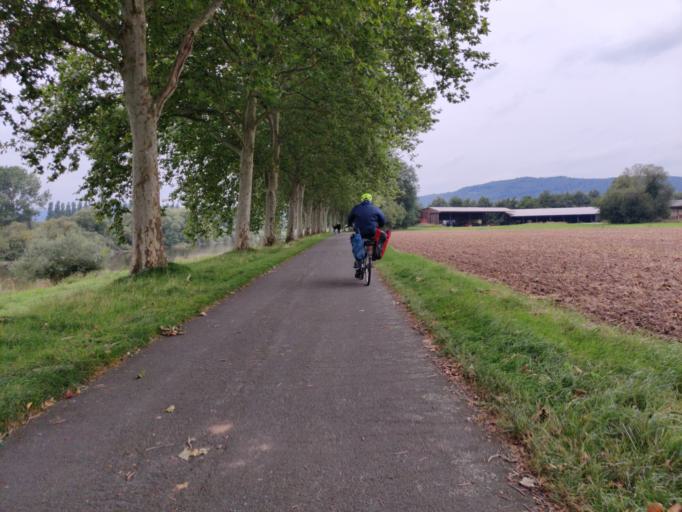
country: DE
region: North Rhine-Westphalia
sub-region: Regierungsbezirk Detmold
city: Hoexter
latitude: 51.7734
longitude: 9.4060
